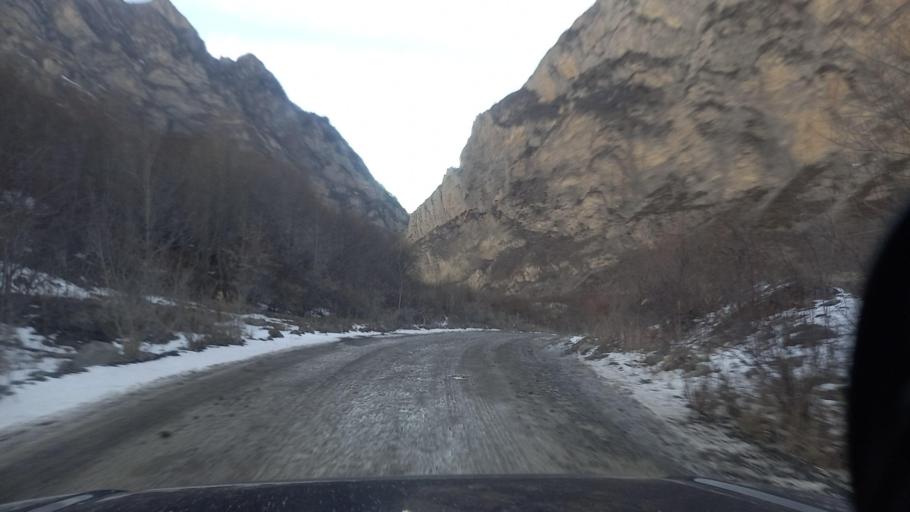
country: RU
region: Ingushetiya
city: Dzhayrakh
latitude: 42.8550
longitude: 44.5205
